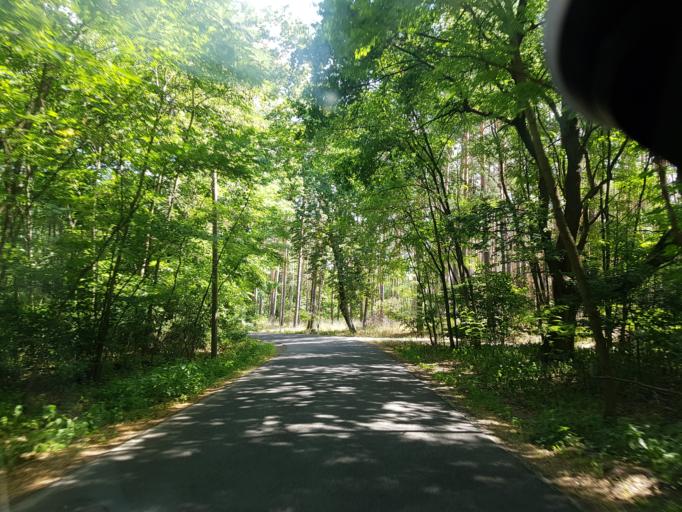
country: DE
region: Brandenburg
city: Cottbus
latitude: 51.6771
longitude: 14.3060
